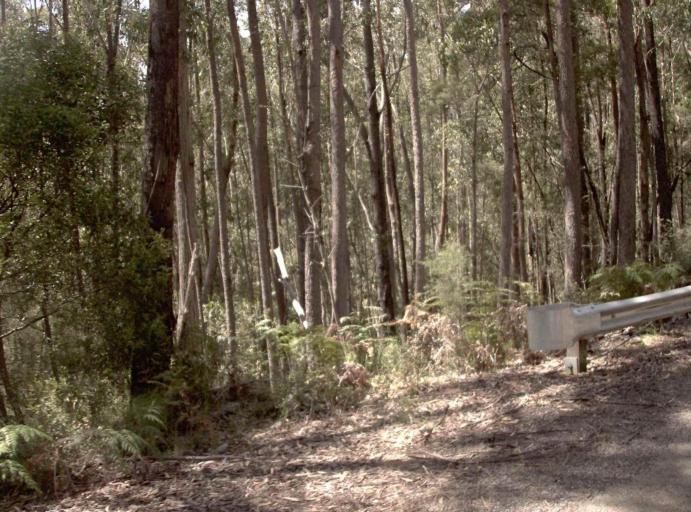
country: AU
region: New South Wales
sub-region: Bombala
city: Bombala
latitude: -37.5698
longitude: 149.3181
